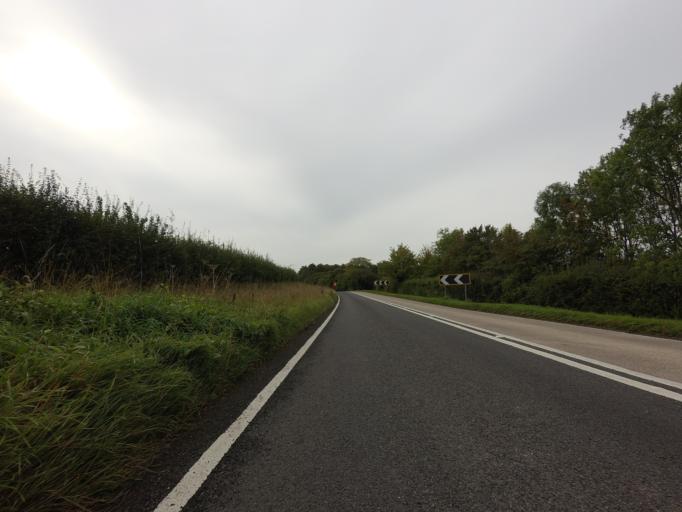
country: GB
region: England
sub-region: Hertfordshire
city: Reed
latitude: 52.0179
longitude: 0.0292
